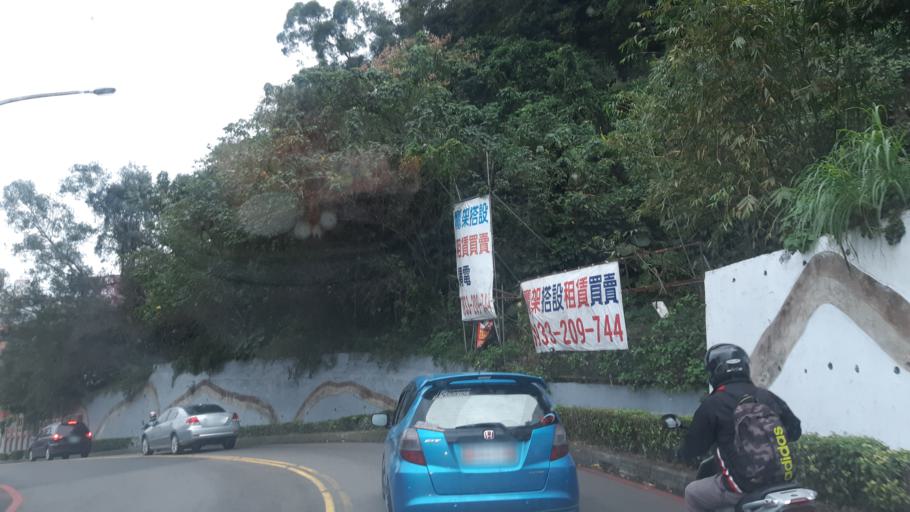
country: TW
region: Taiwan
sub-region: Taoyuan
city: Taoyuan
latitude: 24.9326
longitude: 121.3683
